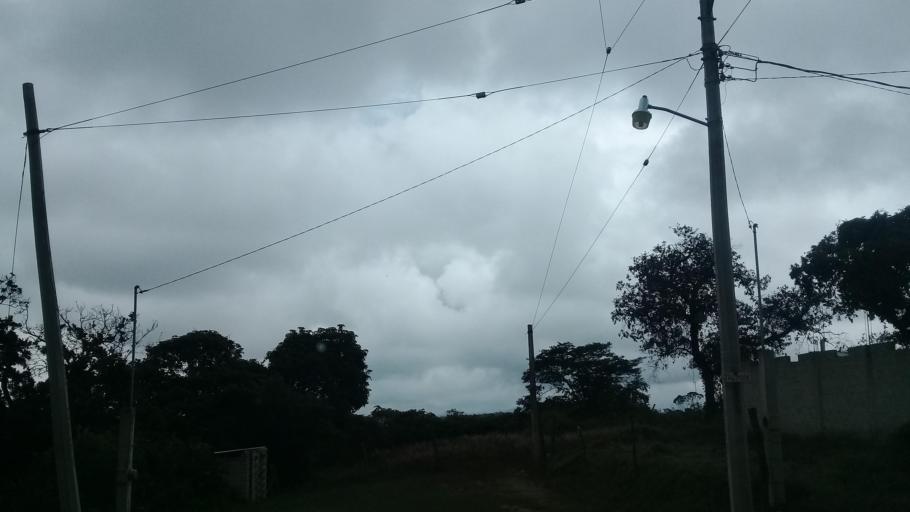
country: MX
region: Veracruz
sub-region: Emiliano Zapata
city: Jacarandas
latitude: 19.4908
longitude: -96.8534
